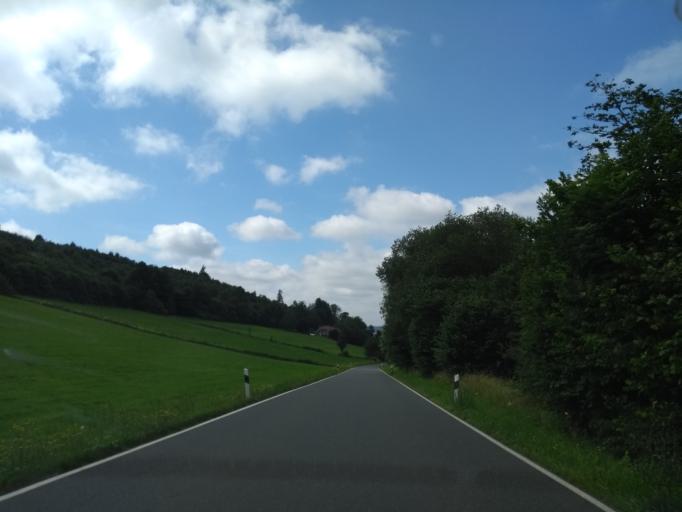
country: DE
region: North Rhine-Westphalia
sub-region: Regierungsbezirk Detmold
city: Lugde
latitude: 51.9518
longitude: 9.2660
